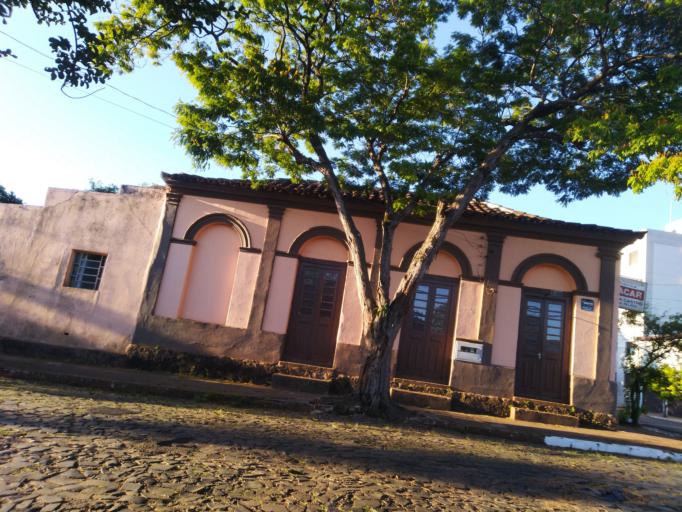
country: BR
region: Rio Grande do Sul
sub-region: Sao Borja
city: Sao Borja
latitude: -28.6615
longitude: -56.0089
